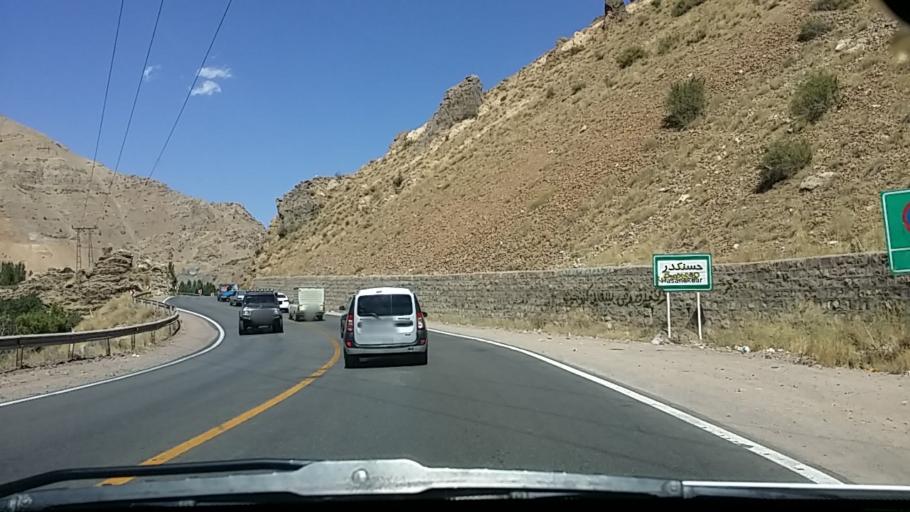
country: IR
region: Tehran
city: Tajrish
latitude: 36.0624
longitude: 51.3094
